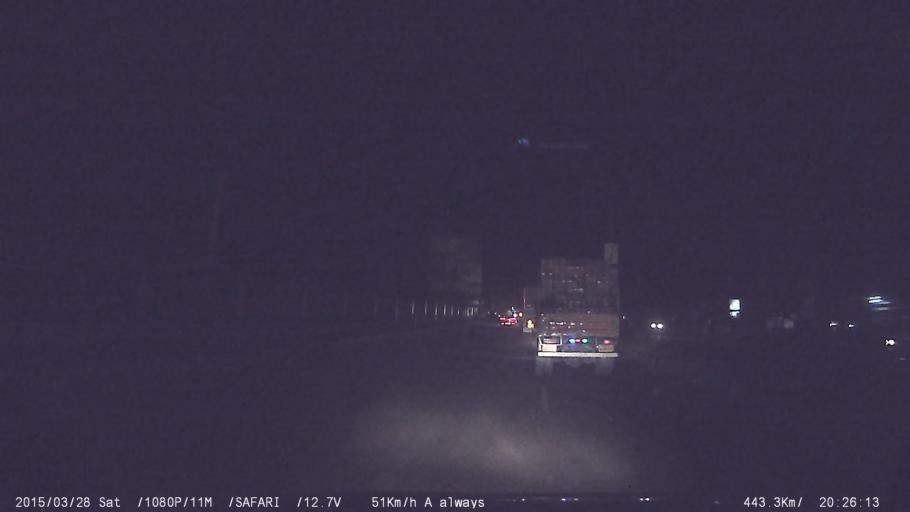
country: IN
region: Karnataka
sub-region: Mandya
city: Maddur
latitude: 12.6031
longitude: 77.0530
